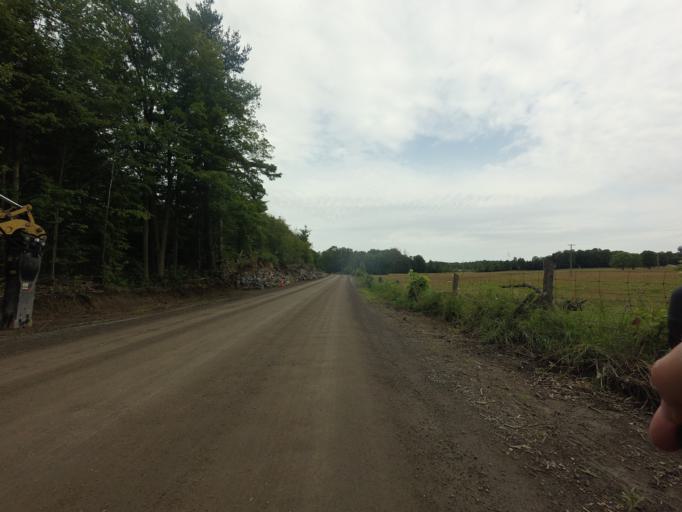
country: CA
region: Ontario
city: Kingston
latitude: 44.5855
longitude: -76.6359
